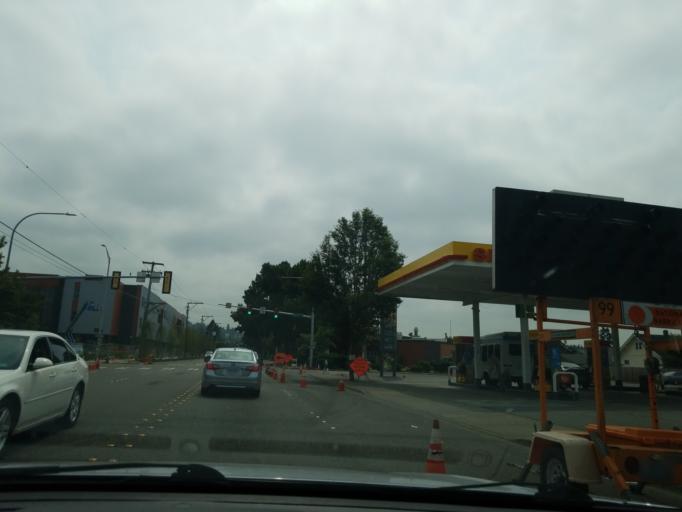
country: US
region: Washington
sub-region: King County
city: Renton
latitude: 47.4890
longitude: -122.2022
